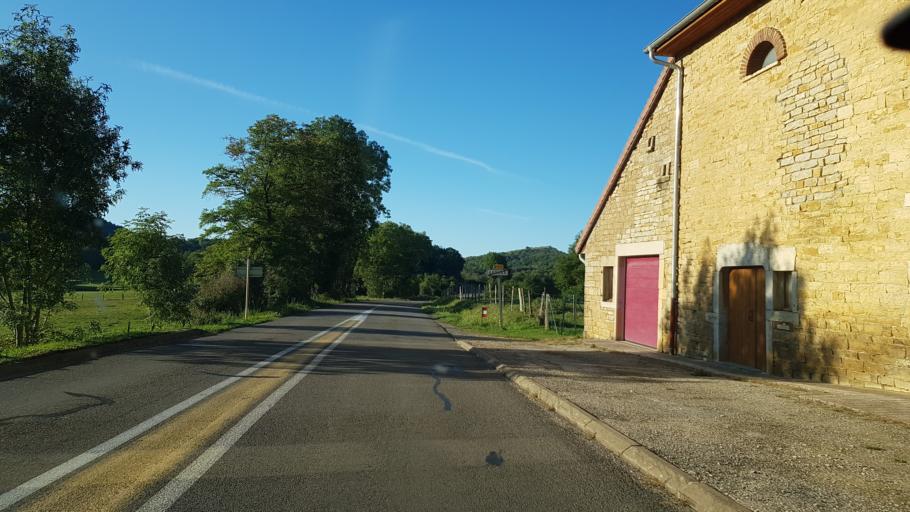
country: FR
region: Franche-Comte
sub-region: Departement du Jura
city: Lons-le-Saunier
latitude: 46.6259
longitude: 5.5296
